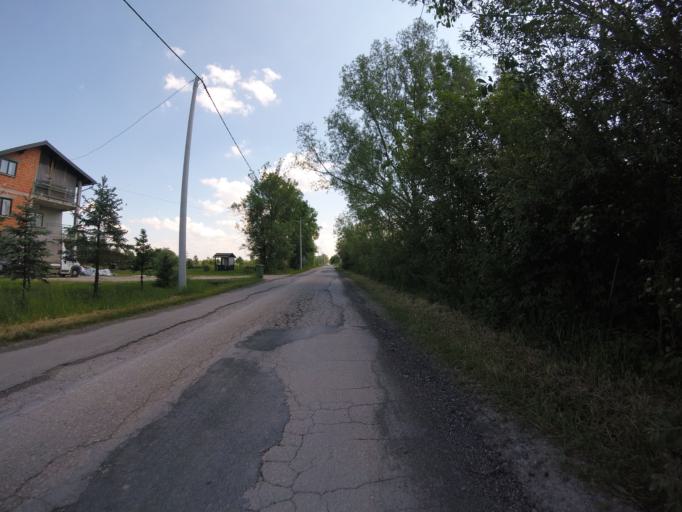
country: HR
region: Zagrebacka
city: Kuce
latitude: 45.6786
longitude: 16.1816
